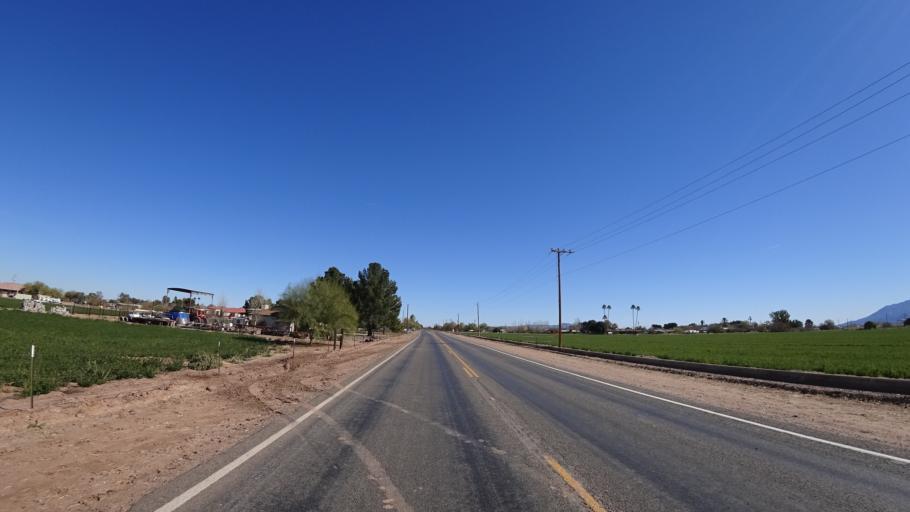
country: US
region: Arizona
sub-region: Maricopa County
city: Avondale
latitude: 33.3918
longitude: -112.3093
